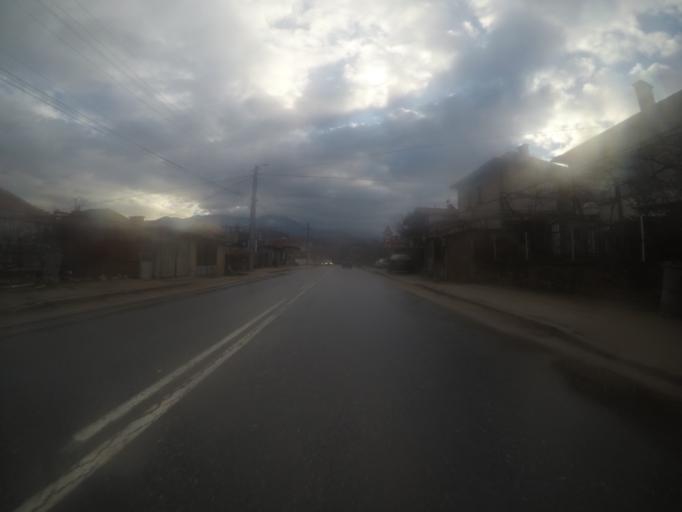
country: BG
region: Blagoevgrad
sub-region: Obshtina Simitli
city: Simitli
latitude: 41.8797
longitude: 23.1265
